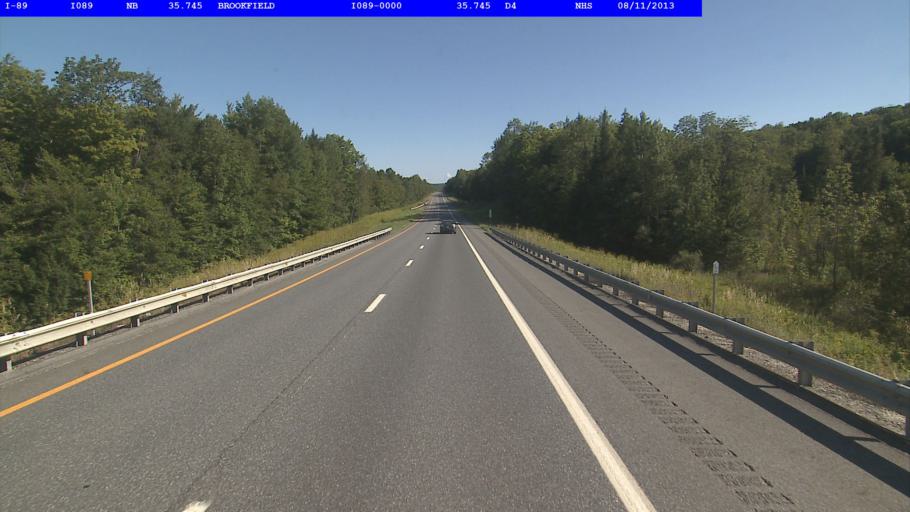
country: US
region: Vermont
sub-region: Orange County
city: Randolph
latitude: 44.0138
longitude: -72.6178
